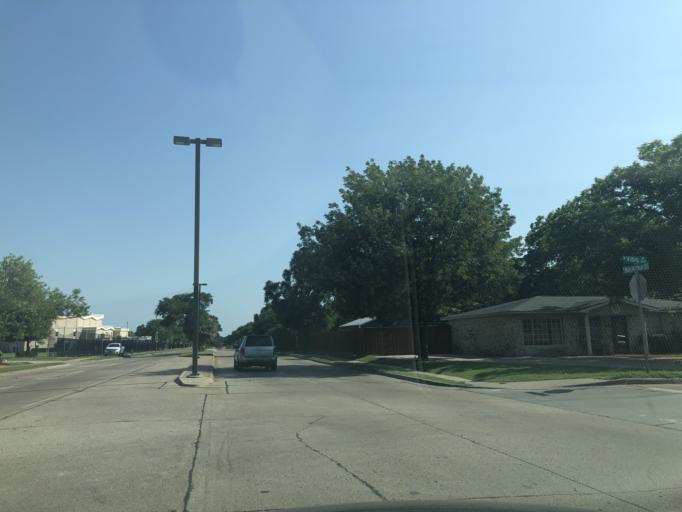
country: US
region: Texas
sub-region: Dallas County
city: Irving
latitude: 32.7974
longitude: -96.9592
